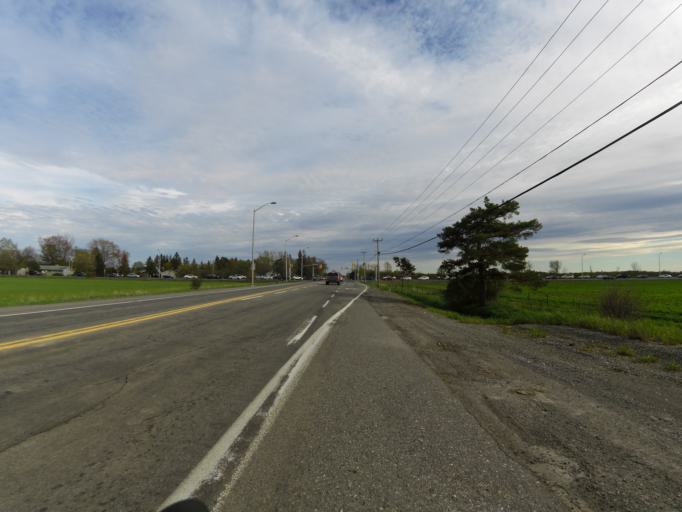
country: CA
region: Ontario
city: Ottawa
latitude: 45.3080
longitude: -75.7089
